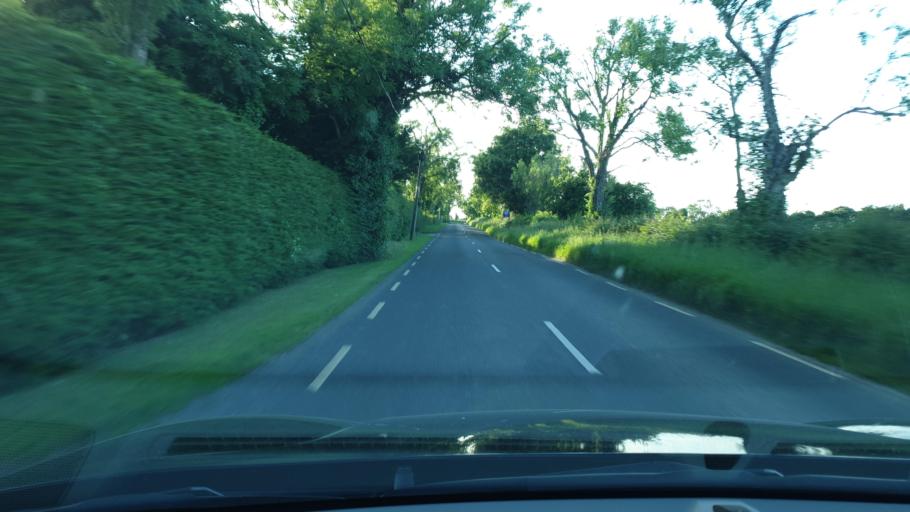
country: IE
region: Leinster
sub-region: An Mhi
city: Ashbourne
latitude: 53.4772
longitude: -6.4268
